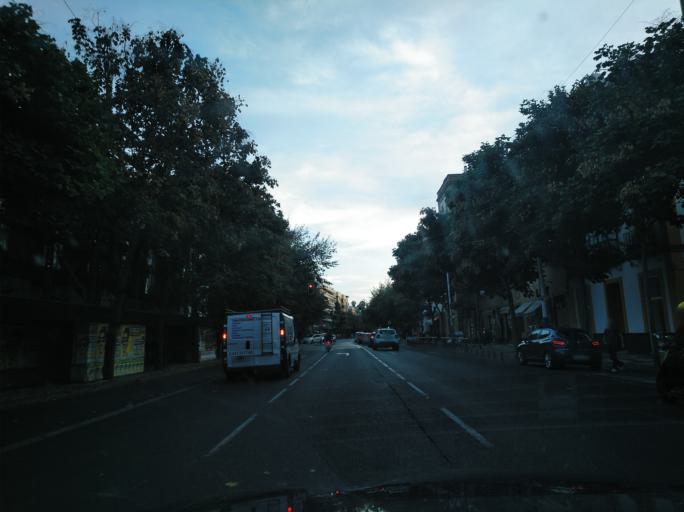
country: ES
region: Andalusia
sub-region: Provincia de Sevilla
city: Sevilla
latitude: 37.3886
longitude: -5.9847
